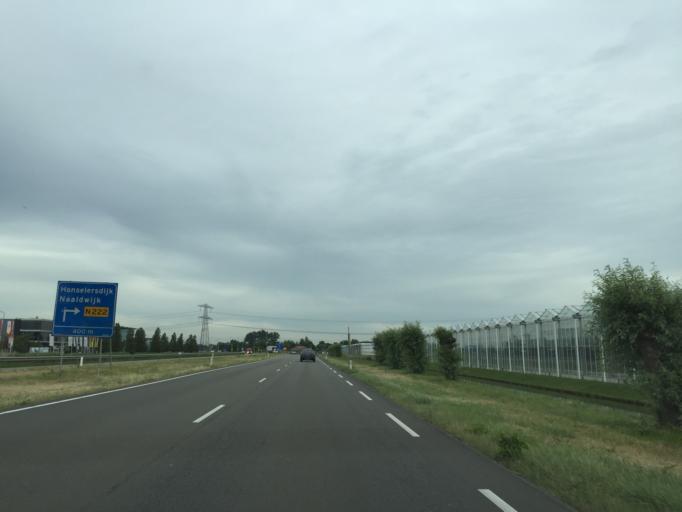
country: NL
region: South Holland
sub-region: Gemeente Westland
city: Kwintsheul
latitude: 52.0123
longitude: 4.2824
